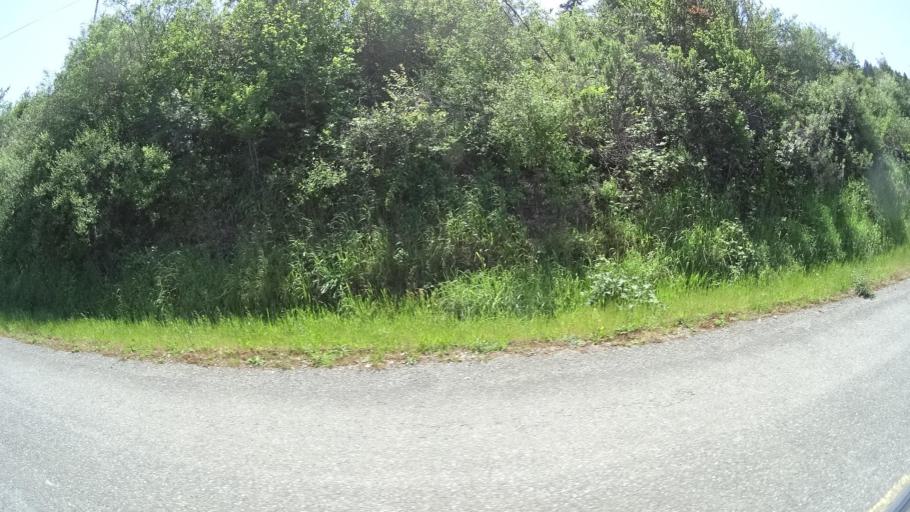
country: US
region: California
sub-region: Humboldt County
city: Redway
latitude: 40.2168
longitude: -123.6409
